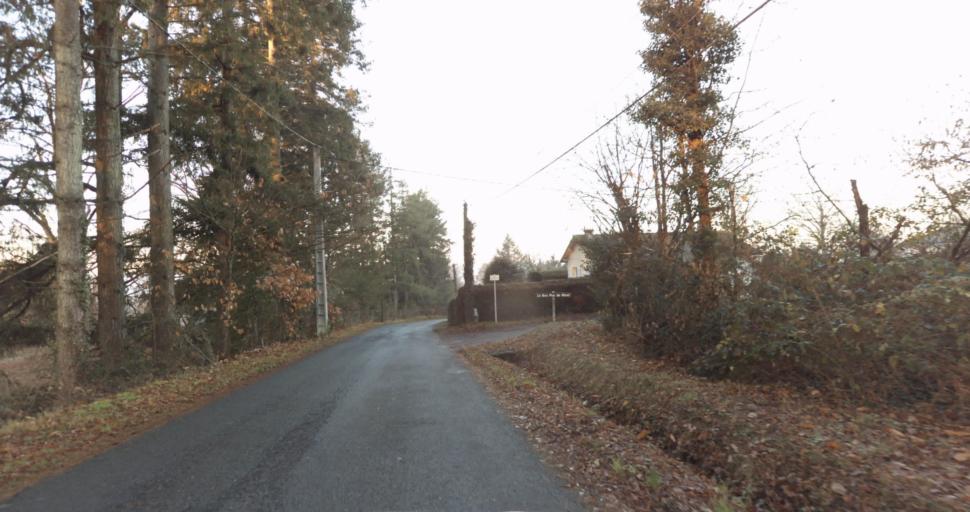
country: FR
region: Limousin
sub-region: Departement de la Haute-Vienne
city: Aixe-sur-Vienne
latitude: 45.8160
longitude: 1.1495
